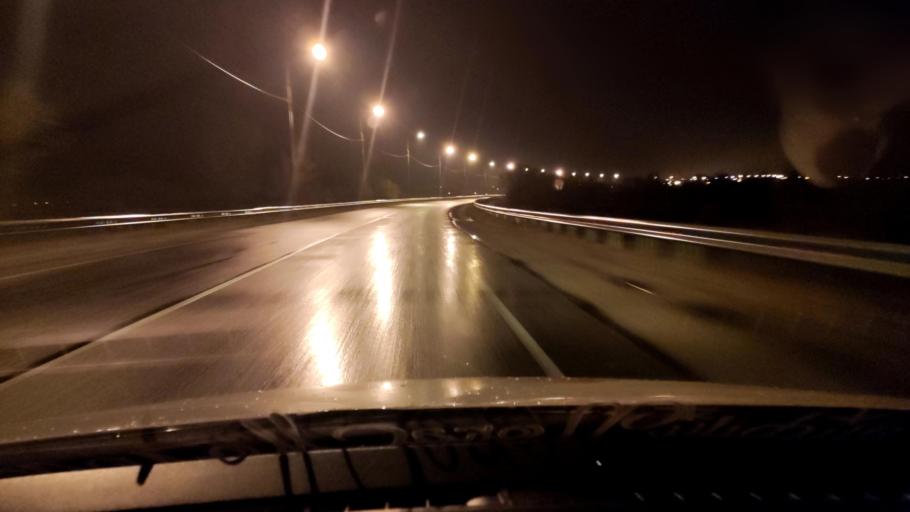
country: RU
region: Voronezj
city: Pridonskoy
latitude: 51.7184
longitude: 39.0731
